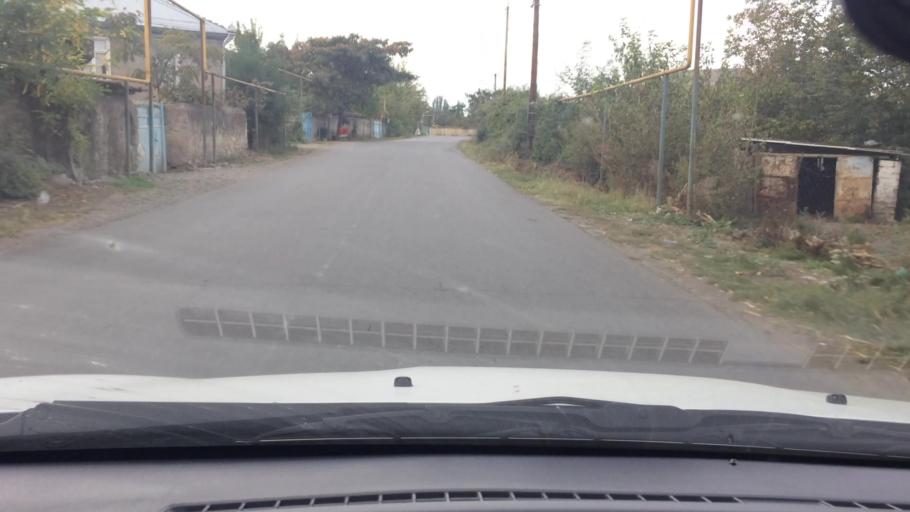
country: GE
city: Naghvarevi
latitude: 41.3513
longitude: 44.8642
